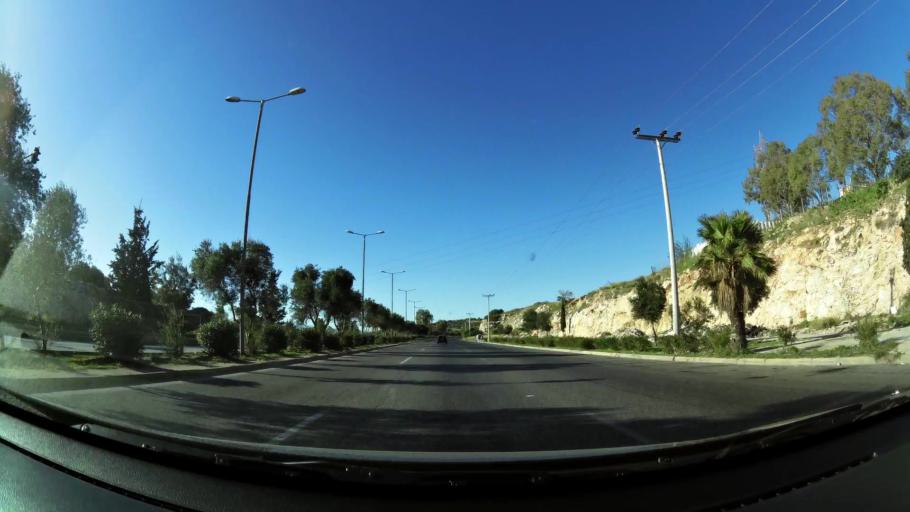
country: GR
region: Attica
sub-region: Nomos Piraios
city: Perama
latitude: 37.9835
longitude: 23.5928
